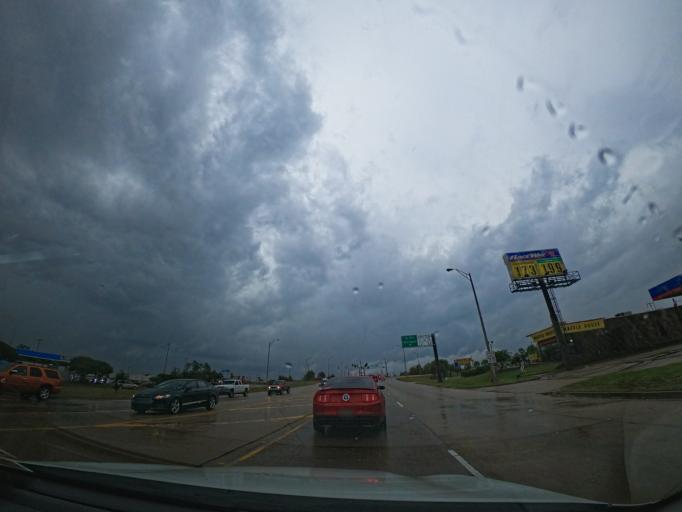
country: US
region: Louisiana
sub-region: Ouachita Parish
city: West Monroe
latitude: 32.5096
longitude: -92.1575
